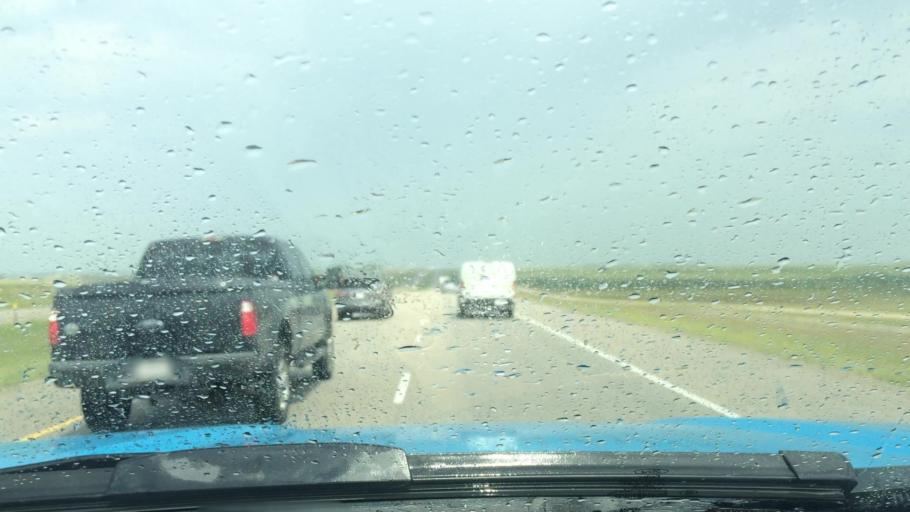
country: CA
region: Alberta
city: Carstairs
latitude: 51.6294
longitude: -114.0253
